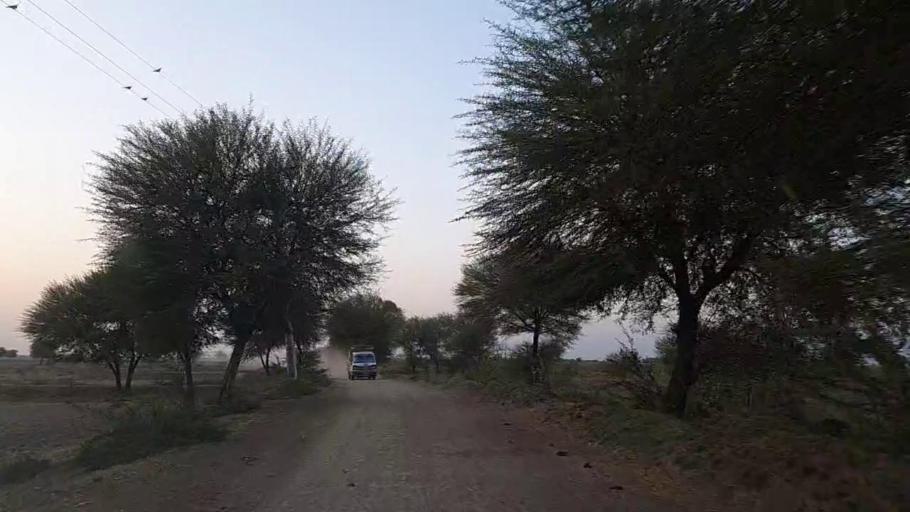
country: PK
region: Sindh
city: Naukot
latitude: 24.8906
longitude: 69.3634
